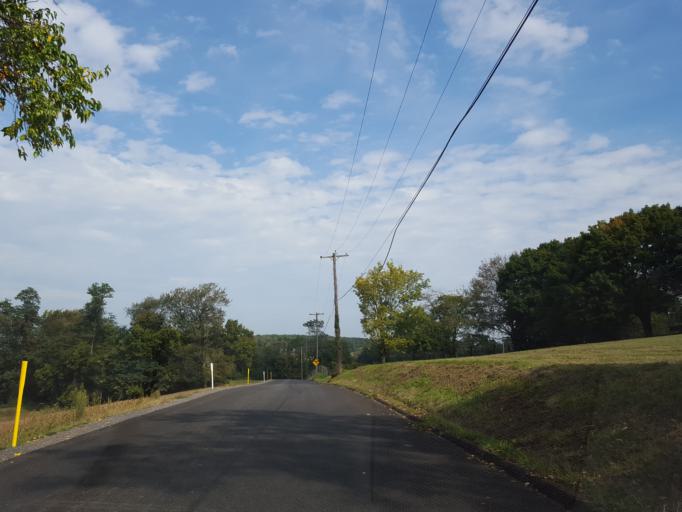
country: US
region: Pennsylvania
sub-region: York County
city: Dallastown
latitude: 39.9076
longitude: -76.6624
